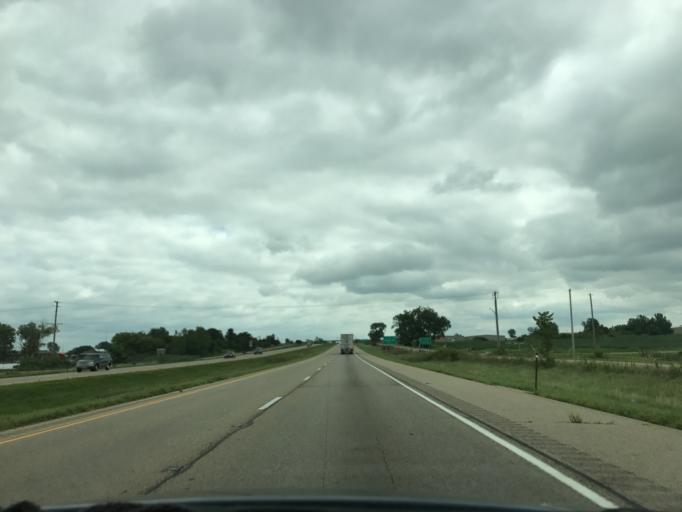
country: US
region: Illinois
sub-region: Bureau County
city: Spring Valley
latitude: 41.3645
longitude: -89.1666
